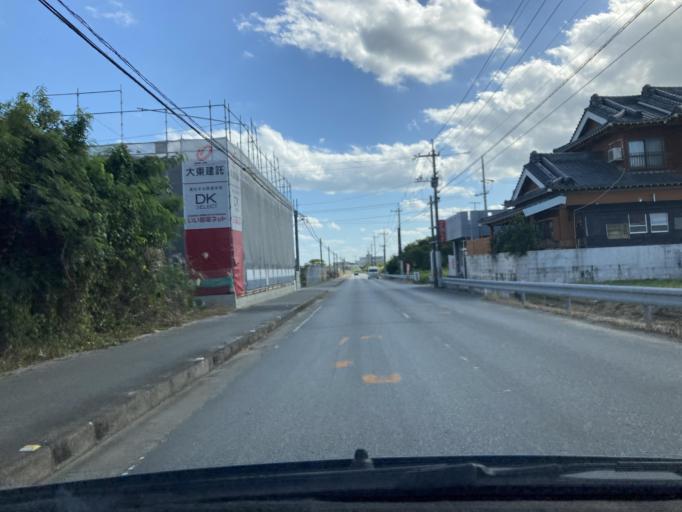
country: JP
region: Okinawa
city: Gushikawa
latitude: 26.3472
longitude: 127.8468
